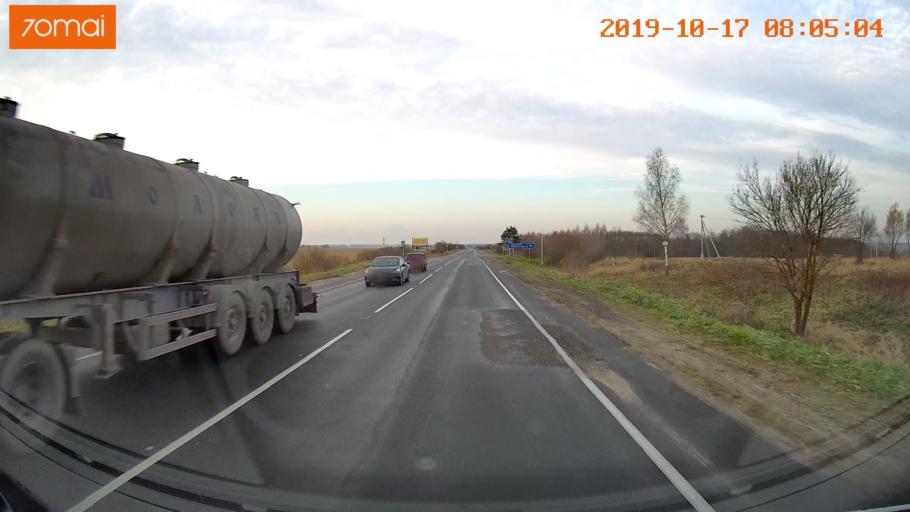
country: RU
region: Vladimir
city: Kol'chugino
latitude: 56.3385
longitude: 39.4226
